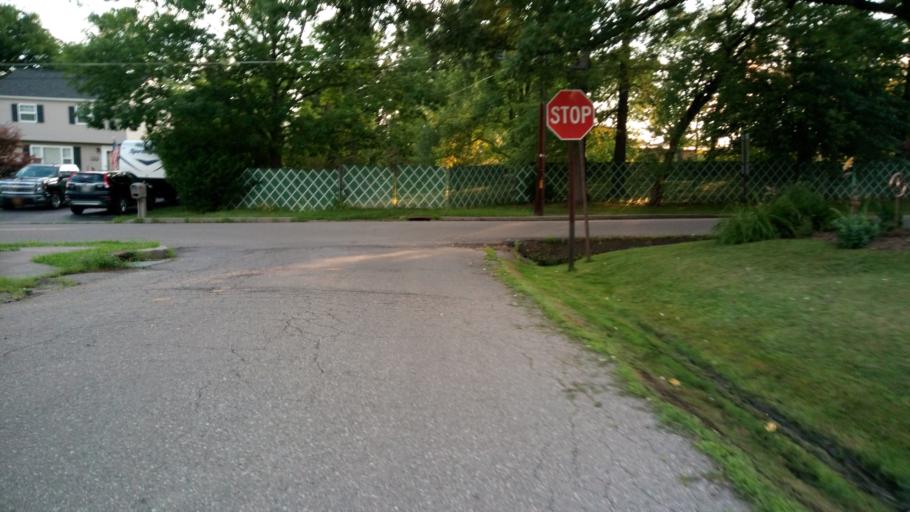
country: US
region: New York
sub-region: Chemung County
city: West Elmira
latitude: 42.0821
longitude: -76.8459
